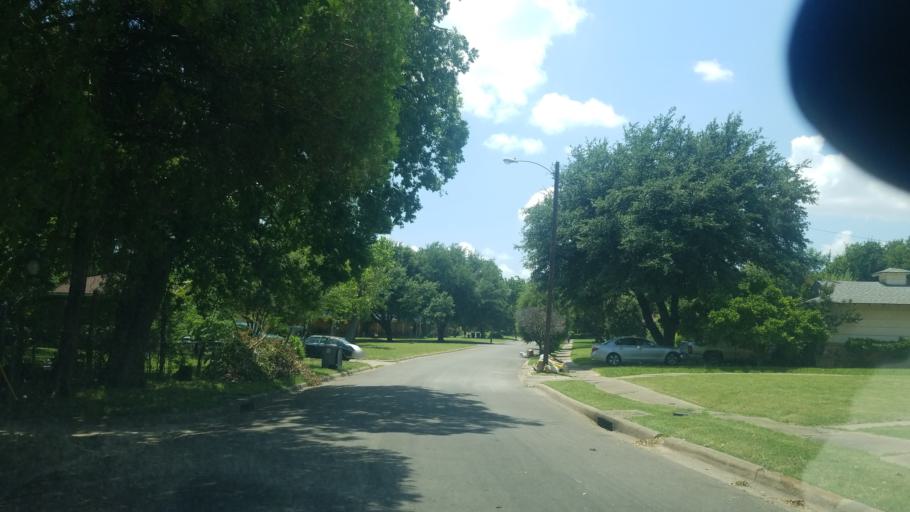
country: US
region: Texas
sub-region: Dallas County
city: Dallas
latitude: 32.7205
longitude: -96.7861
